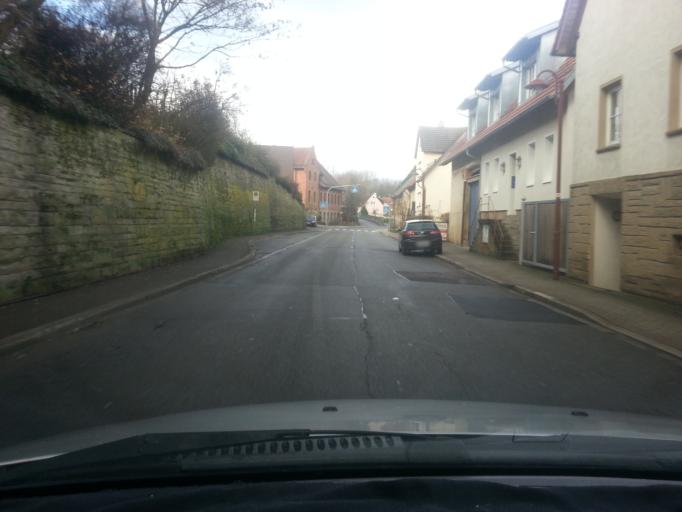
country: DE
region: Baden-Wuerttemberg
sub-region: Karlsruhe Region
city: Balzfeld
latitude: 49.2119
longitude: 8.8045
